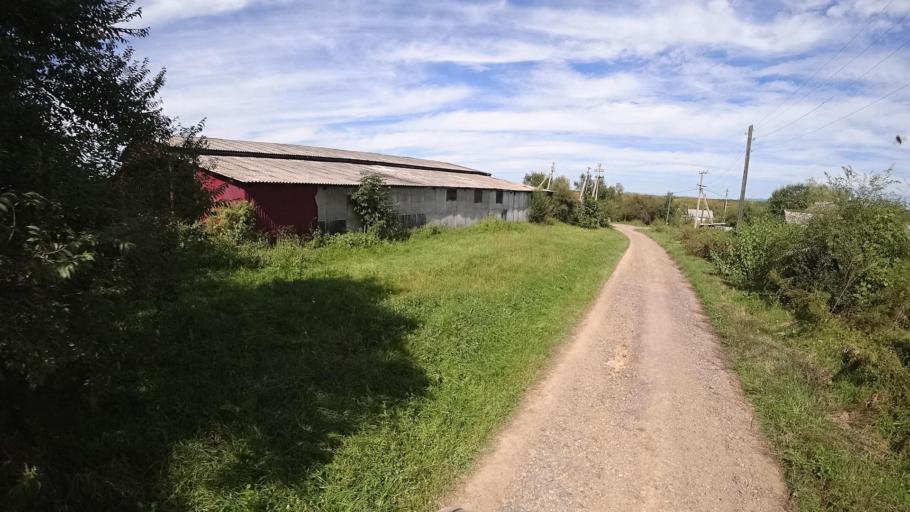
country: RU
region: Primorskiy
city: Yakovlevka
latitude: 44.4342
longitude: 133.5594
